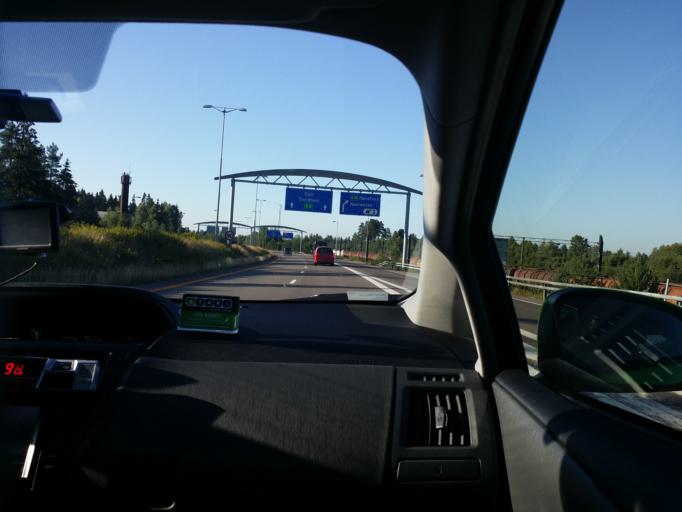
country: NO
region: Akershus
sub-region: Nannestad
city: Teigebyen
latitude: 60.1833
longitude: 11.0930
